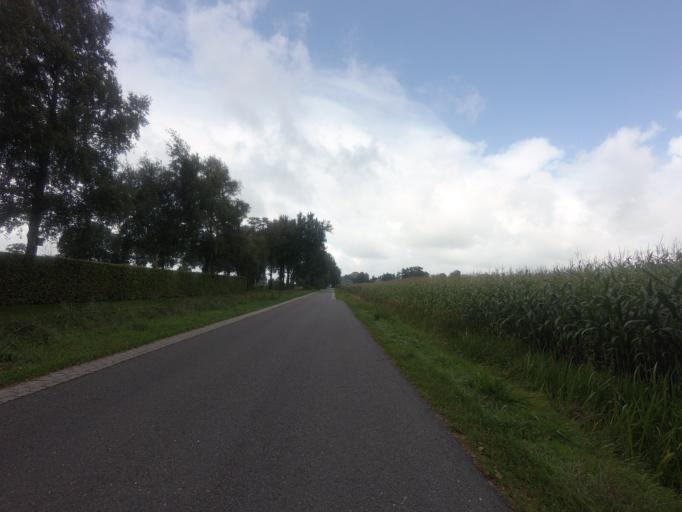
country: NL
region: Friesland
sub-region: Gemeente Skarsterlan
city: Oudehaske
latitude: 52.9347
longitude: 5.8527
